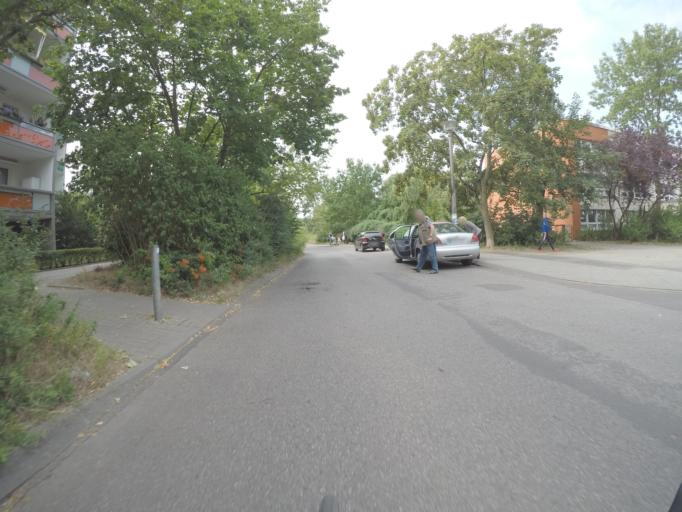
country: DE
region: Berlin
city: Buch
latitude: 52.6319
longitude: 13.4931
